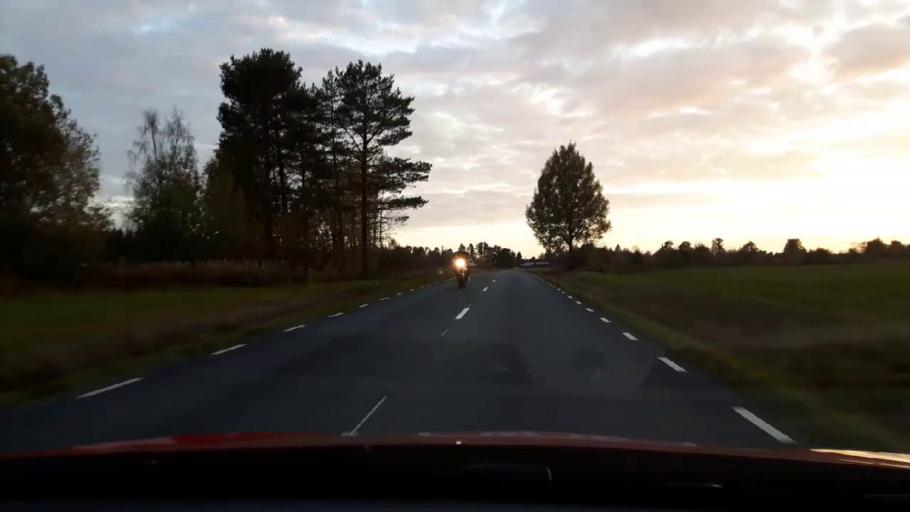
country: SE
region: Jaemtland
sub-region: OEstersunds Kommun
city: Ostersund
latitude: 63.2440
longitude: 14.5832
